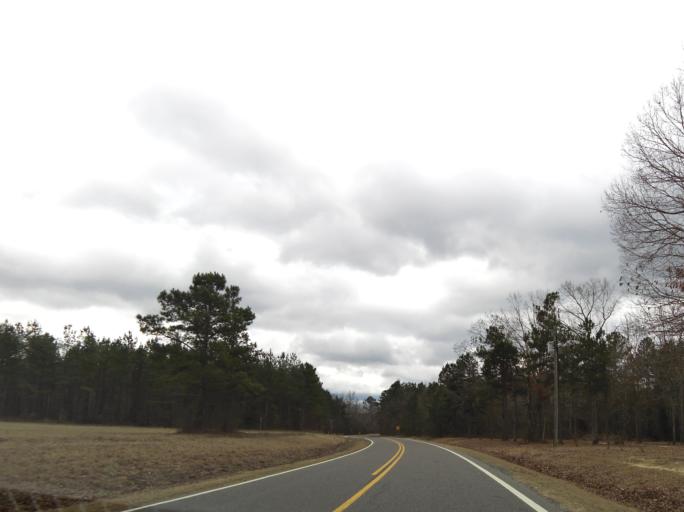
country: US
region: Georgia
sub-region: Bleckley County
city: Cochran
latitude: 32.5104
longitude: -83.3679
